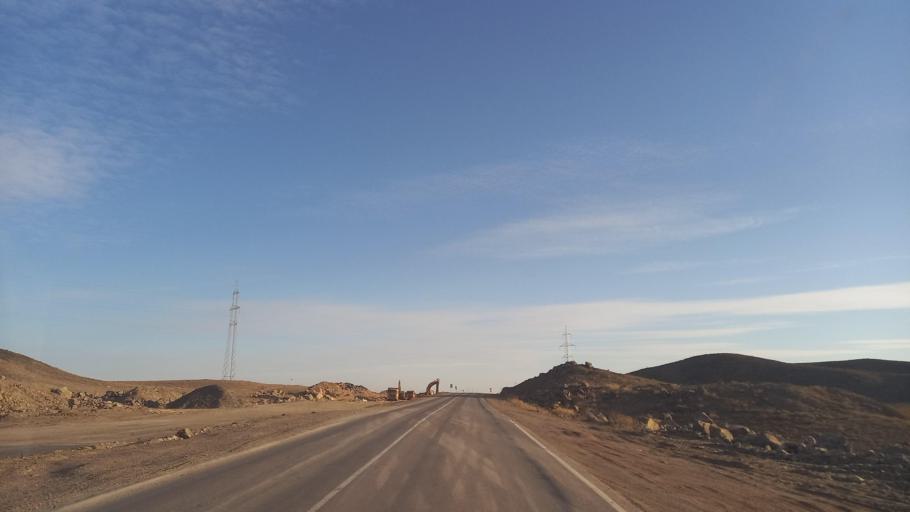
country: KZ
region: Zhambyl
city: Mynaral
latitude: 45.3530
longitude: 73.6852
